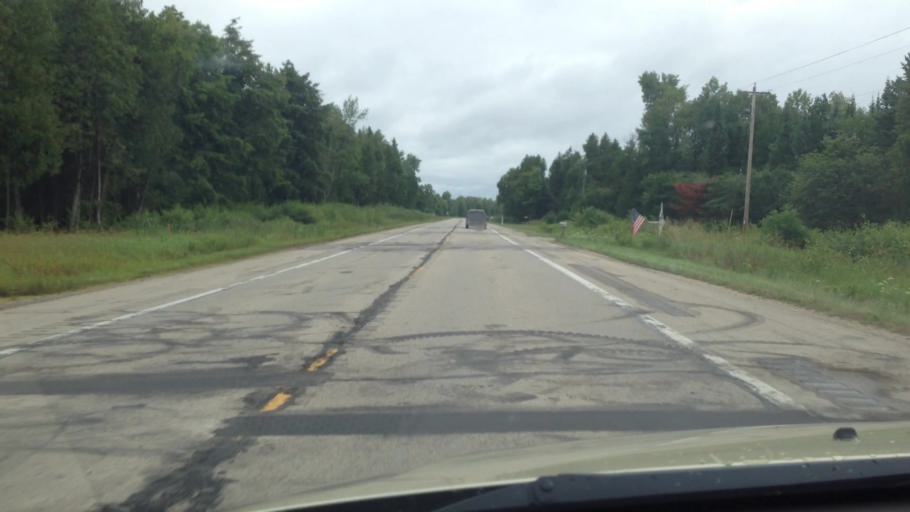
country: US
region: Michigan
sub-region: Delta County
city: Escanaba
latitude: 45.6551
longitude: -87.1775
